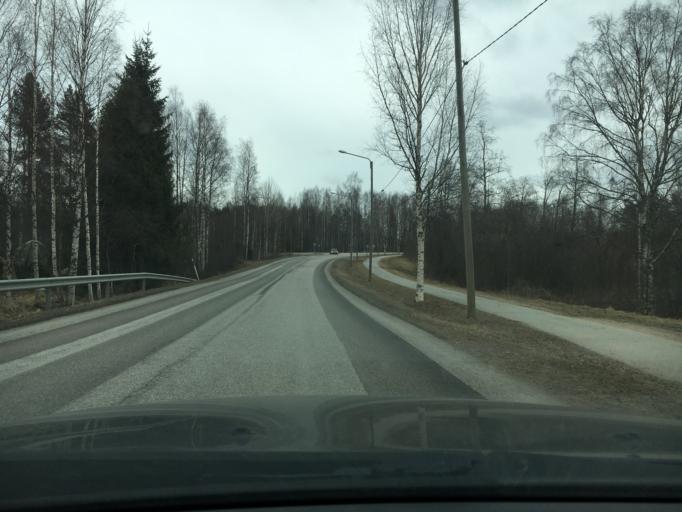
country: FI
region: Central Finland
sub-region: AEaenekoski
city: Suolahti
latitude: 62.5627
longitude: 25.8827
